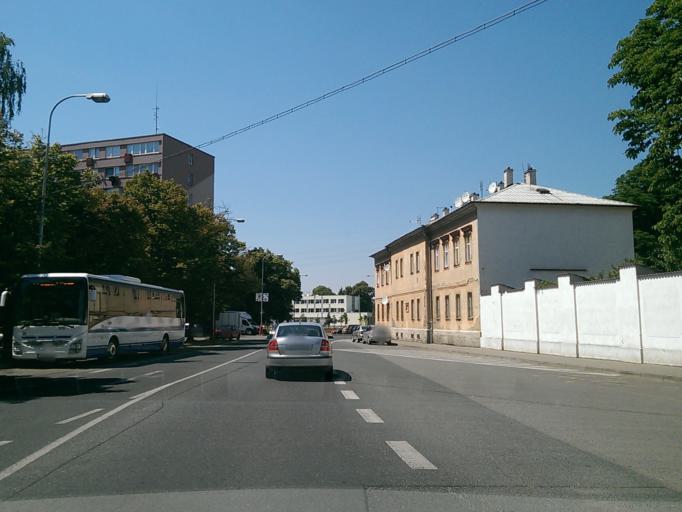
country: CZ
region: Central Bohemia
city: Benatky nad Jizerou
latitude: 50.2859
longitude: 14.8277
